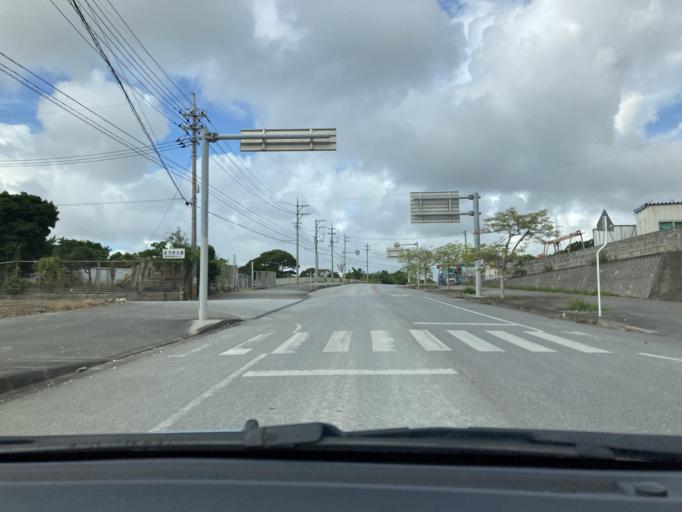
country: JP
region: Okinawa
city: Itoman
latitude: 26.1198
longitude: 127.6918
